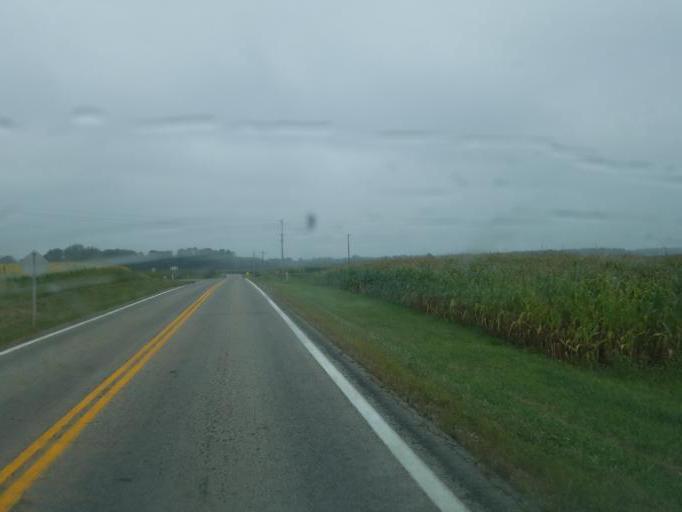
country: US
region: Ohio
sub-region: Knox County
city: Centerburg
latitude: 40.4192
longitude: -82.7021
